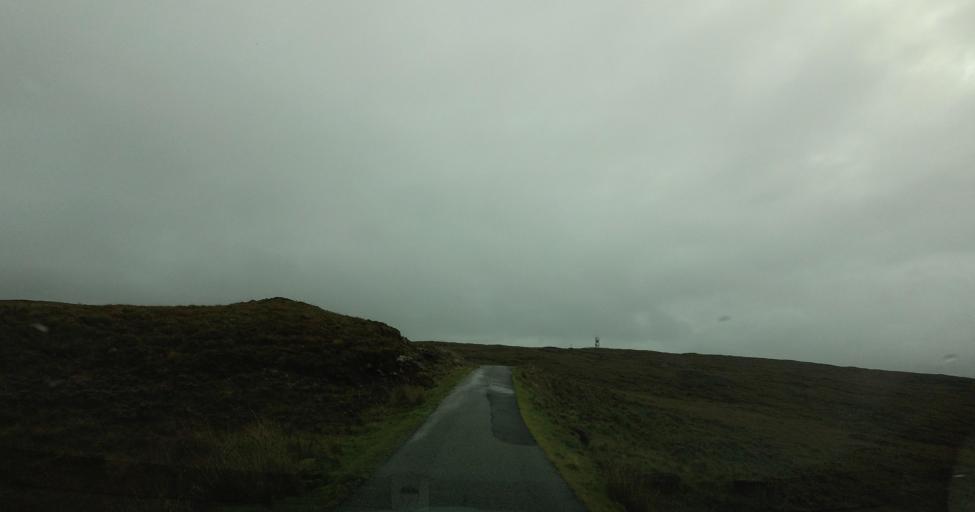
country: GB
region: Scotland
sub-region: Highland
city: Isle of Skye
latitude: 57.1429
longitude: -6.0876
